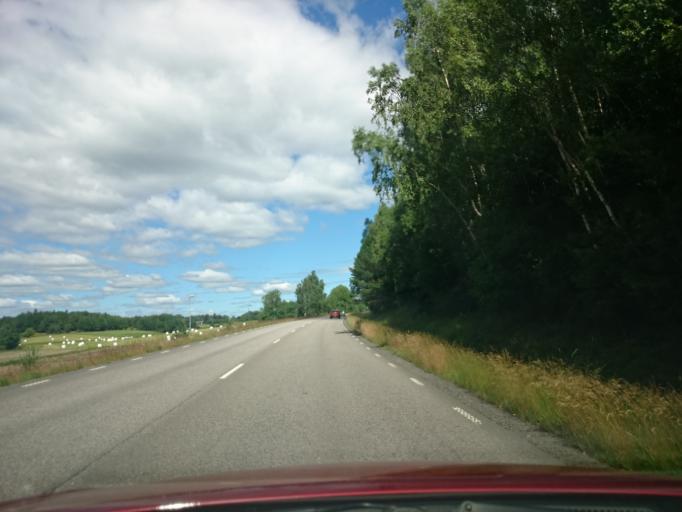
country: SE
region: Vaestra Goetaland
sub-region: Lerums Kommun
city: Stenkullen
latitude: 57.8080
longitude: 12.3029
